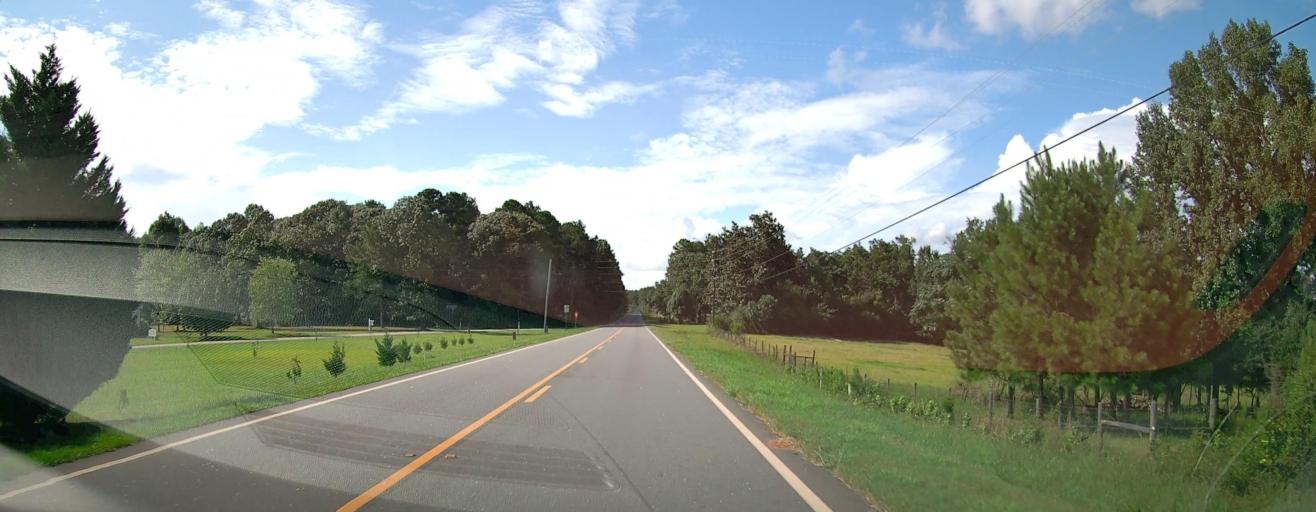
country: US
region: Georgia
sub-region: Upson County
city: Hannahs Mill
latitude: 32.9097
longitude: -84.4262
